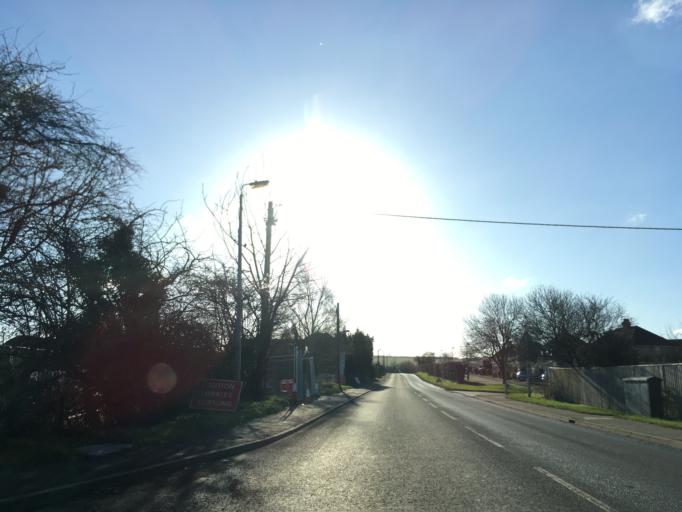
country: GB
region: England
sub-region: Borough of Swindon
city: Wroughton
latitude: 51.5311
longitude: -1.7852
